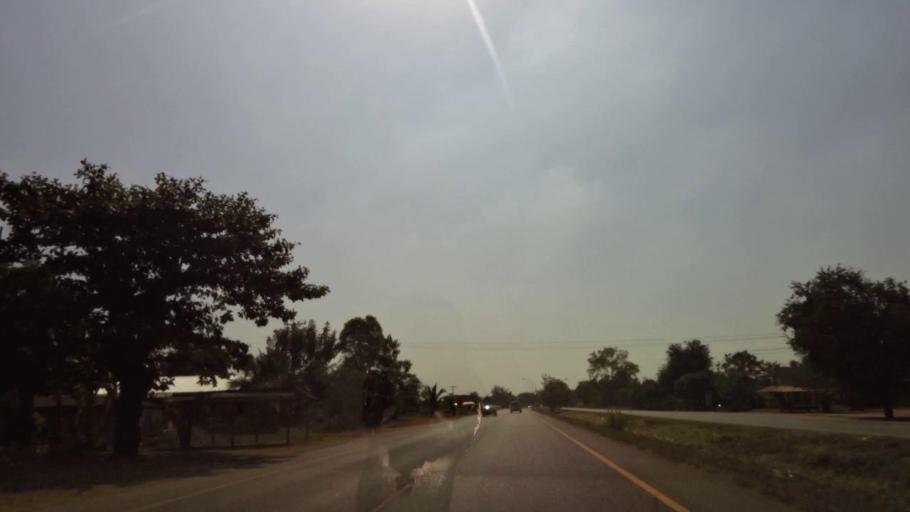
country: TH
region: Phichit
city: Wachira Barami
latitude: 16.3746
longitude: 100.1339
